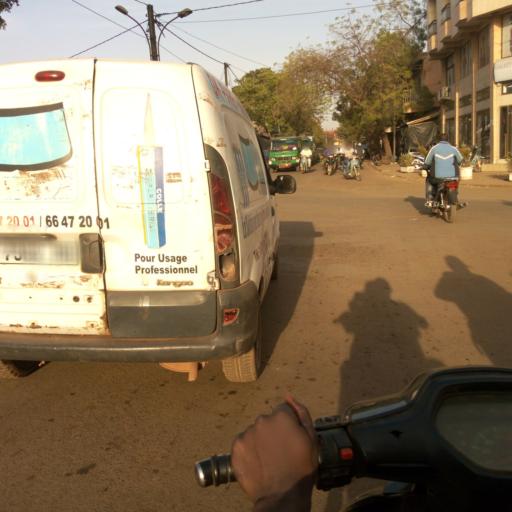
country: ML
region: Bamako
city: Bamako
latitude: 12.6429
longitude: -8.0026
